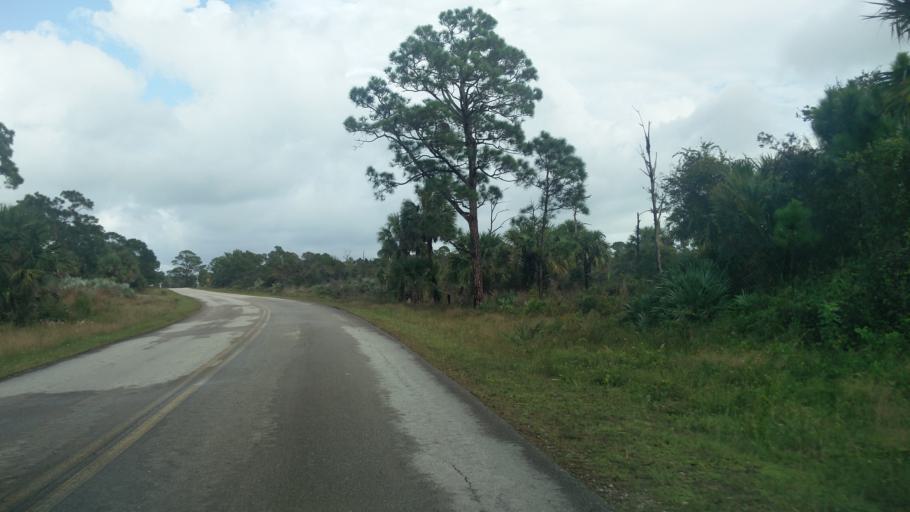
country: US
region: Florida
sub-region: Palm Beach County
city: Tequesta
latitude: 27.0107
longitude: -80.1160
